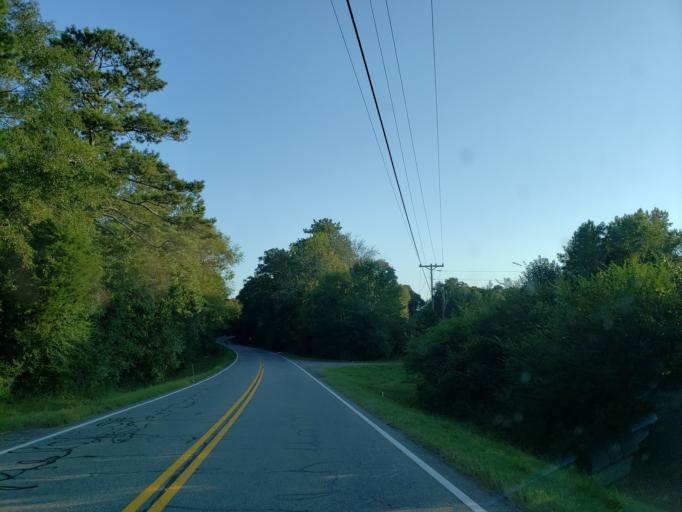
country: US
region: Georgia
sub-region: Gordon County
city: Calhoun
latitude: 34.5521
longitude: -84.8946
